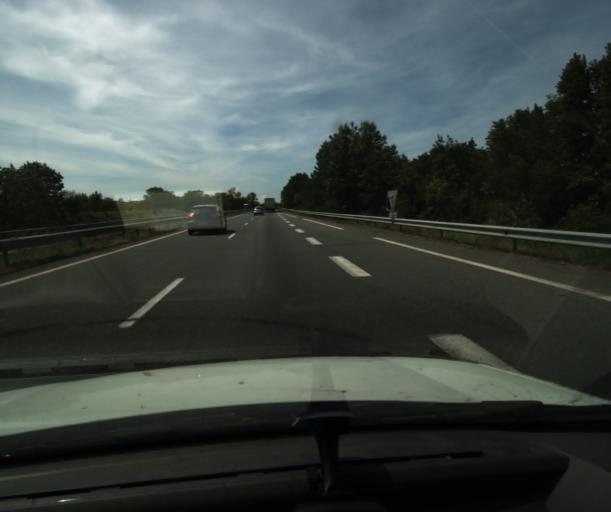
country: FR
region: Languedoc-Roussillon
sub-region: Departement de l'Aude
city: Villeneuve-la-Comptal
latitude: 43.2908
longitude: 1.9386
